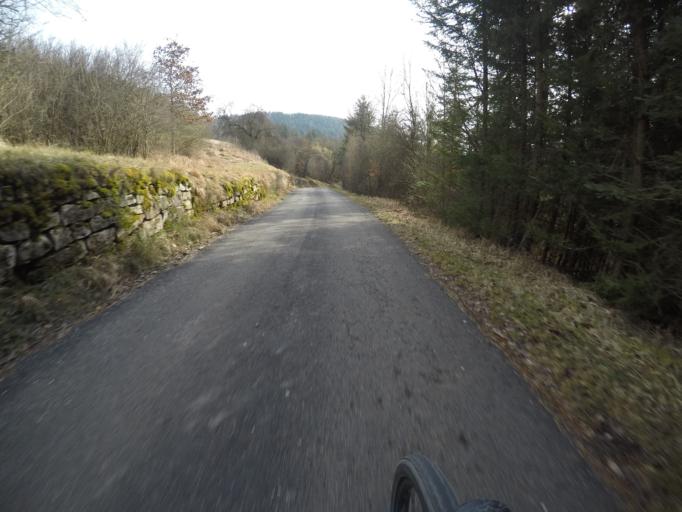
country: DE
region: Baden-Wuerttemberg
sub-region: Karlsruhe Region
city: Wildberg
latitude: 48.6330
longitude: 8.7683
